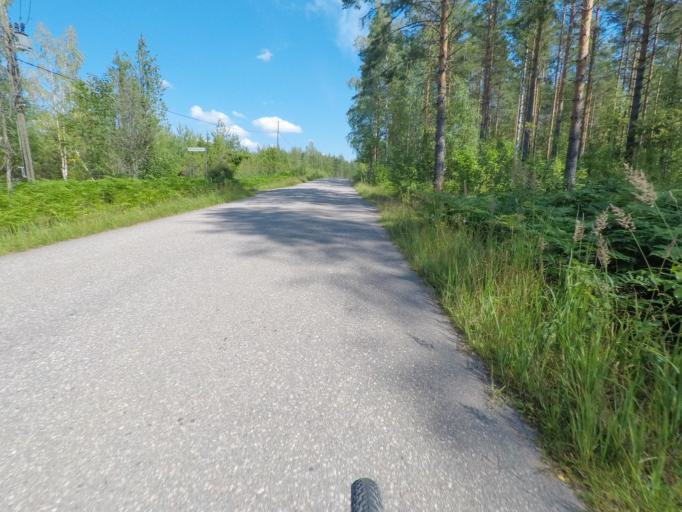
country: FI
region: Southern Savonia
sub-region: Mikkeli
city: Puumala
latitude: 61.4221
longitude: 28.1242
